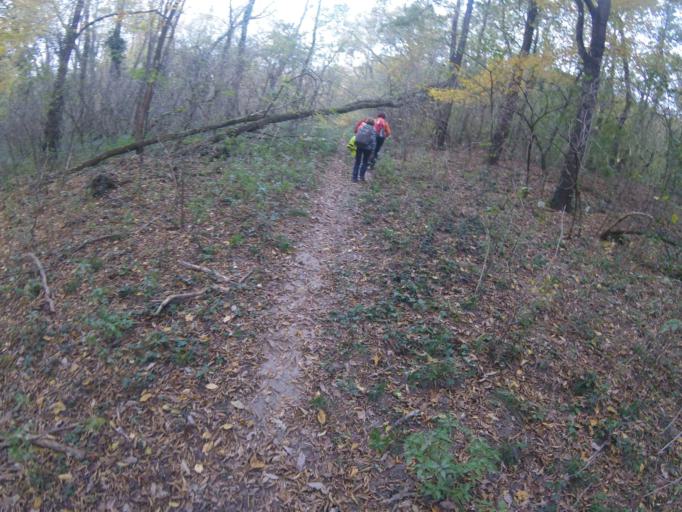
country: HU
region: Fejer
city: Bodajk
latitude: 47.3176
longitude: 18.2123
